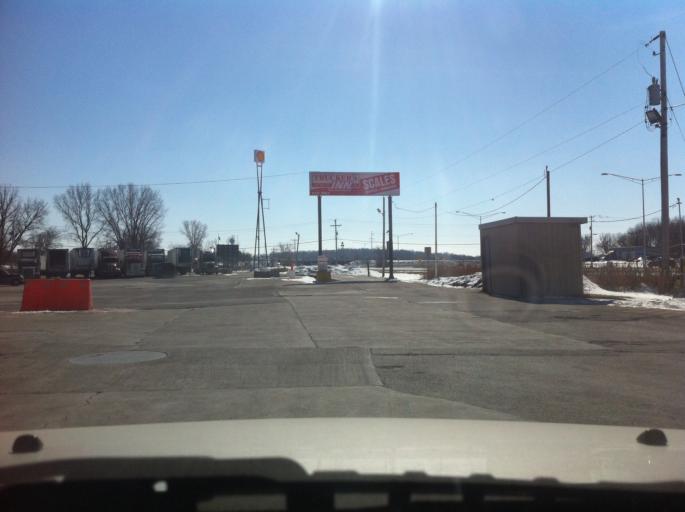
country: US
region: Wisconsin
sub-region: Dane County
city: Windsor
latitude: 43.1845
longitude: -89.3237
